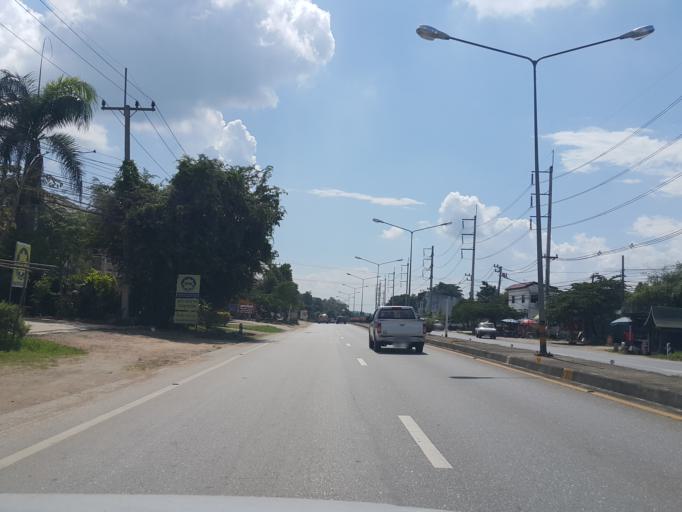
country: TH
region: Chiang Mai
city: Mae Taeng
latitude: 19.1350
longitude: 98.9487
